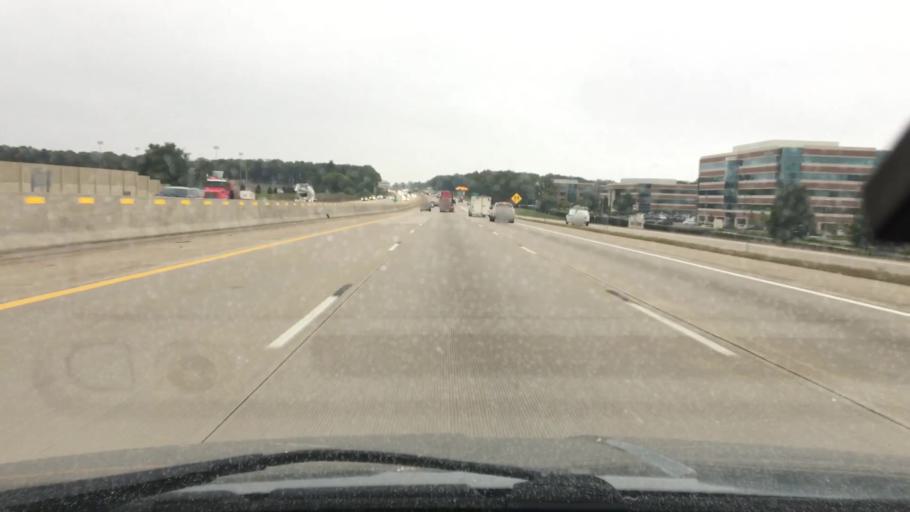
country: US
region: Michigan
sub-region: Kalamazoo County
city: Portage
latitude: 42.2368
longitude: -85.5932
